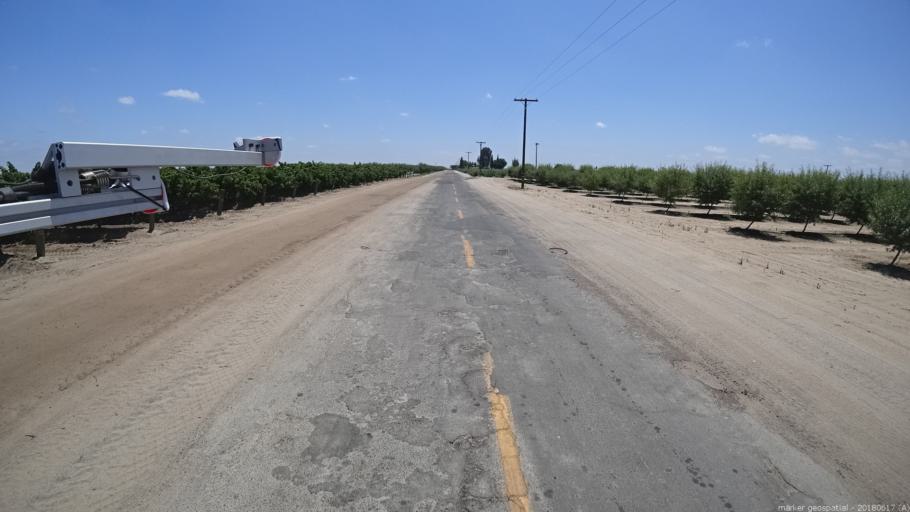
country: US
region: California
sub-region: Fresno County
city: Kerman
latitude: 36.8157
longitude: -120.1509
